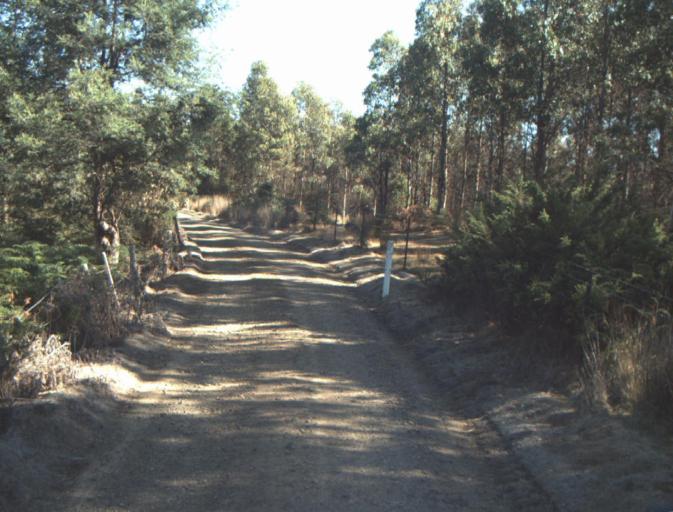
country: AU
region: Tasmania
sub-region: Dorset
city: Scottsdale
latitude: -41.3028
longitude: 147.3587
